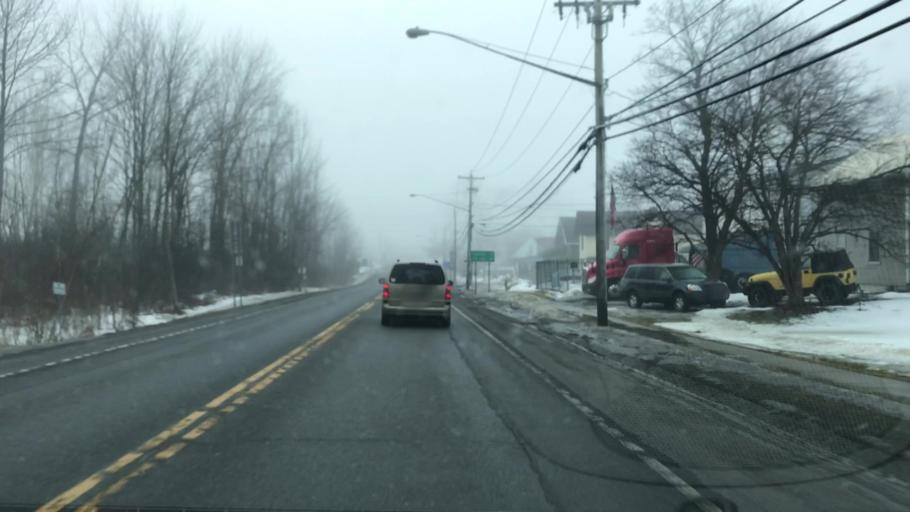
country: US
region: New York
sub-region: Washington County
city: Whitehall
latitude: 43.5429
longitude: -73.4079
